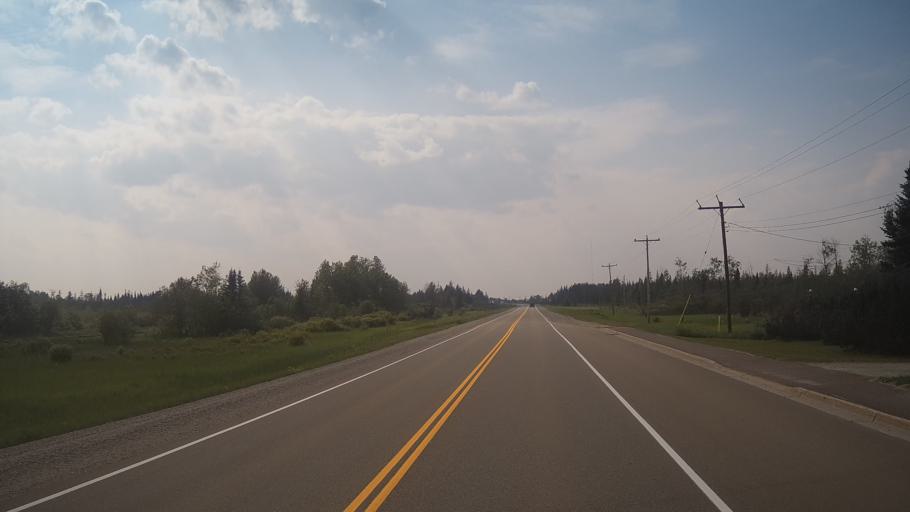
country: CA
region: Ontario
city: Kapuskasing
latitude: 49.4758
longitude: -82.6847
